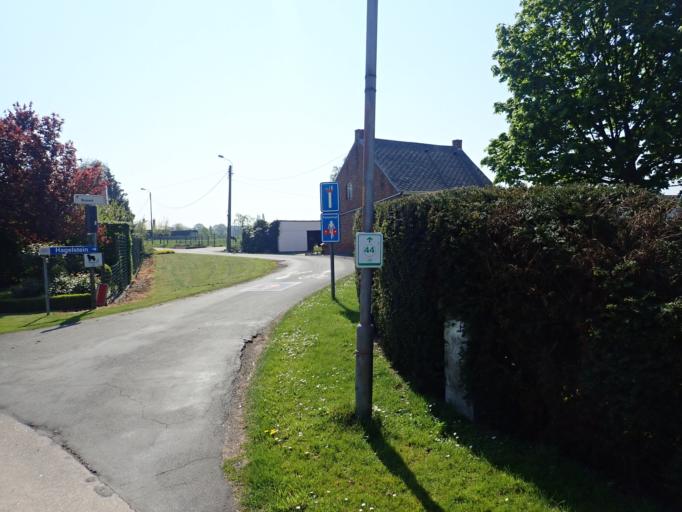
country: BE
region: Flanders
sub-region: Provincie Antwerpen
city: Sint-Katelijne-Waver
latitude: 51.0601
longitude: 4.5334
